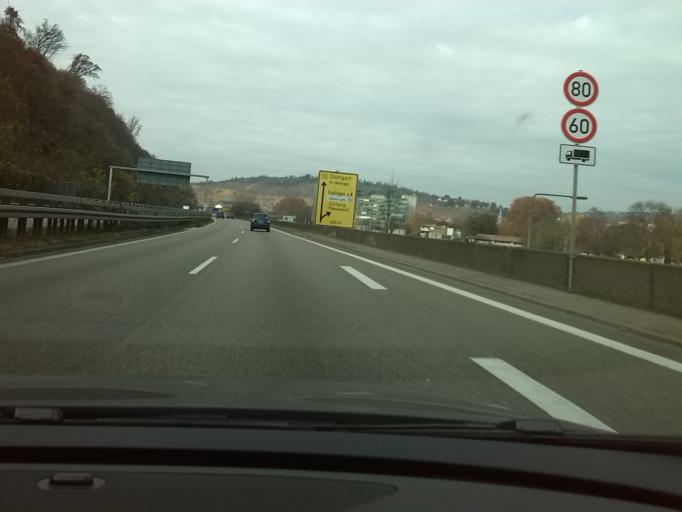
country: DE
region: Baden-Wuerttemberg
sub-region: Regierungsbezirk Stuttgart
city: Esslingen
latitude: 48.7297
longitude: 9.3157
